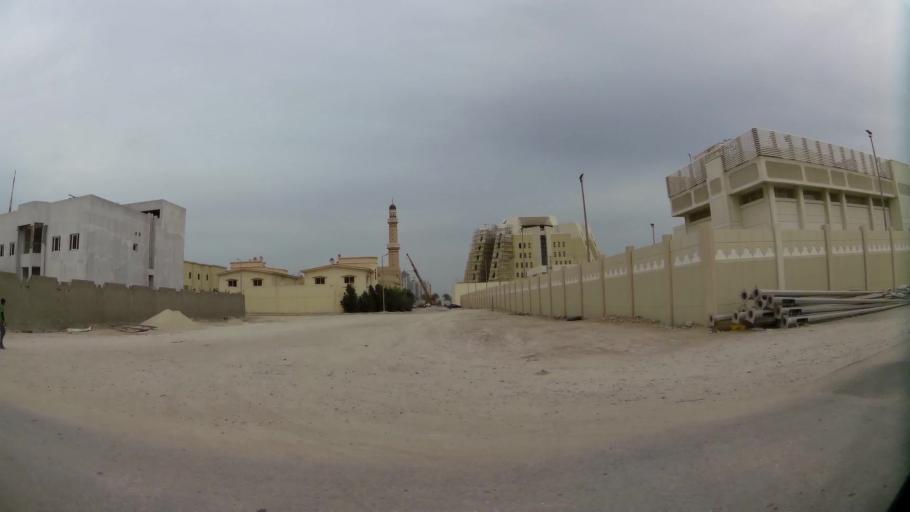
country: QA
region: Baladiyat ad Dawhah
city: Doha
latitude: 25.3071
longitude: 51.5018
